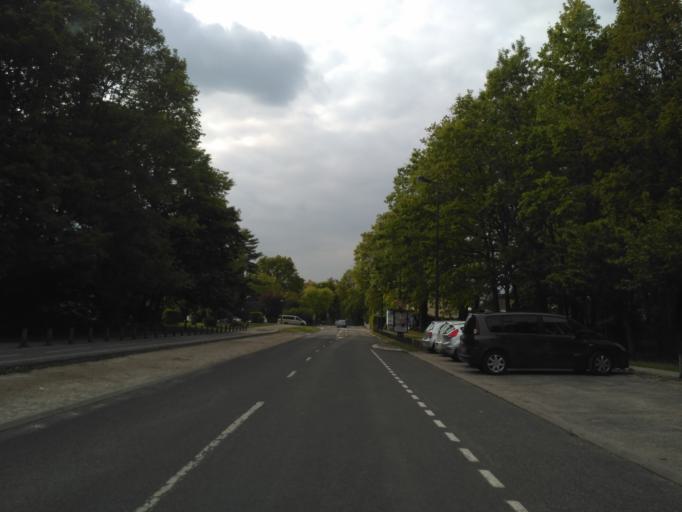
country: FR
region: Ile-de-France
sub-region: Departement de Seine-et-Marne
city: Cesson
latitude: 48.5574
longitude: 2.5976
